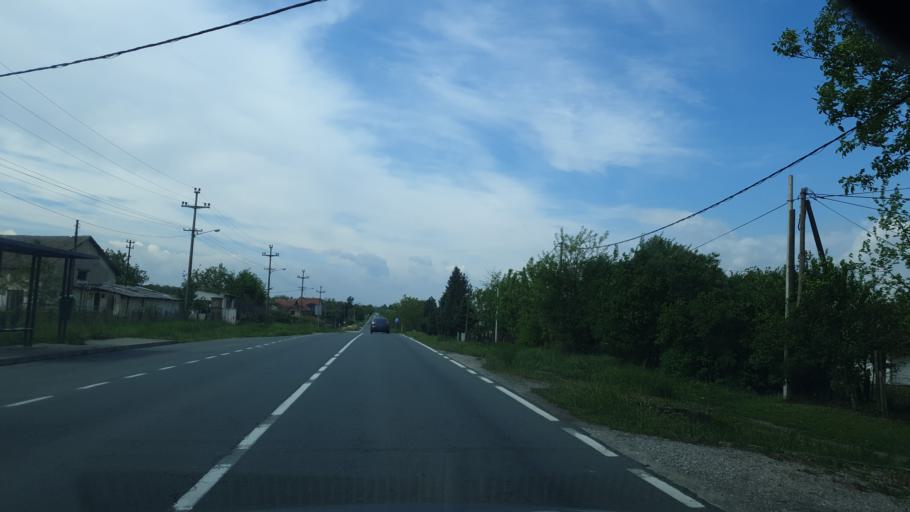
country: RS
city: Stubline
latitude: 44.5790
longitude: 20.1528
